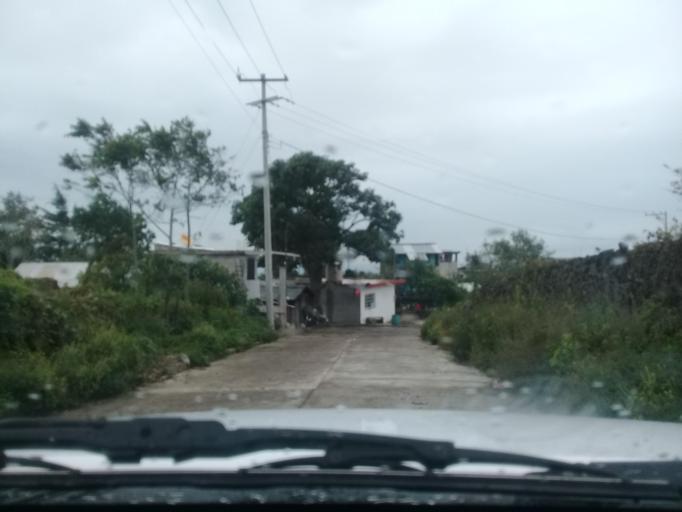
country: MX
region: Veracruz
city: Rafael Lucio
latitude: 19.6162
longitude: -96.9931
